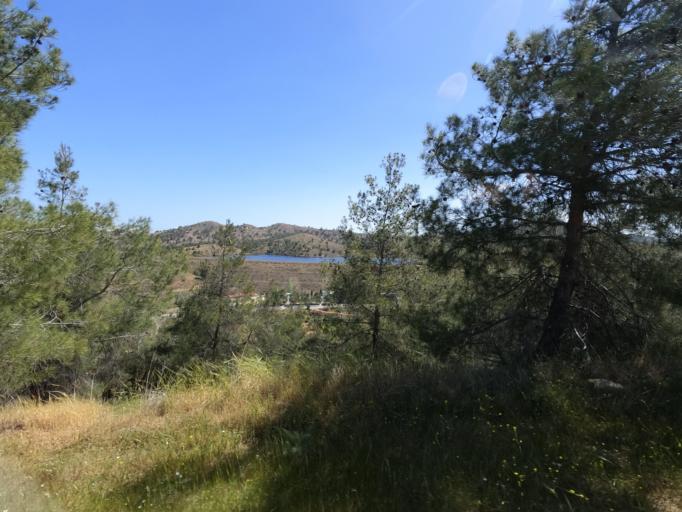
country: CY
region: Lefkosia
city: Astromeritis
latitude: 35.0594
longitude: 33.0234
